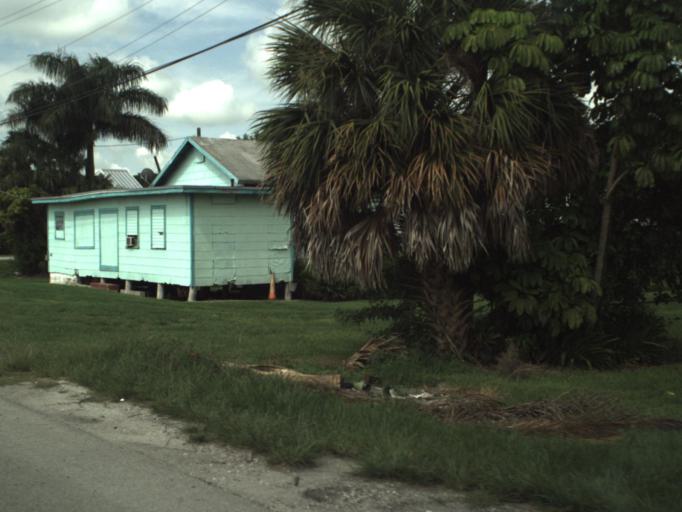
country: US
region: Florida
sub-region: Palm Beach County
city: Belle Glade
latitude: 26.6802
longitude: -80.6853
